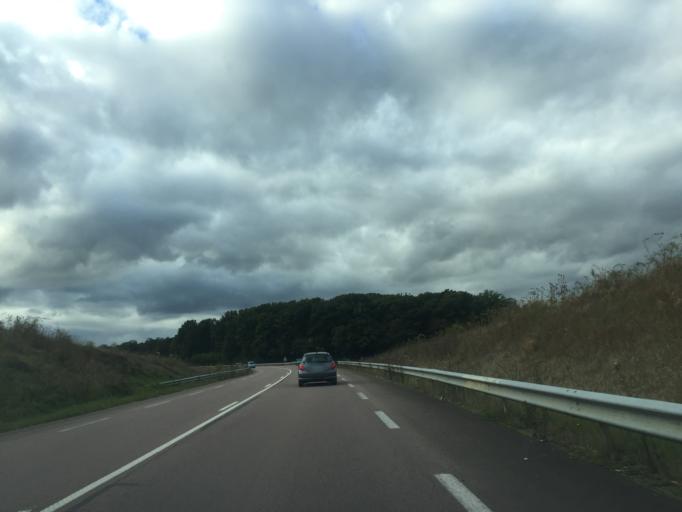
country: FR
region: Lorraine
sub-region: Departement des Vosges
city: Chatenois
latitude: 48.2979
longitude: 5.8828
